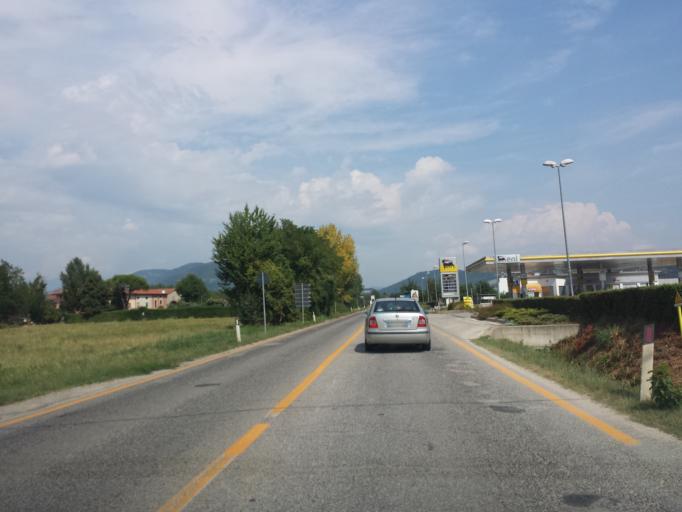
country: IT
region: Veneto
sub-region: Provincia di Vicenza
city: Trissino
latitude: 45.5702
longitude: 11.3839
